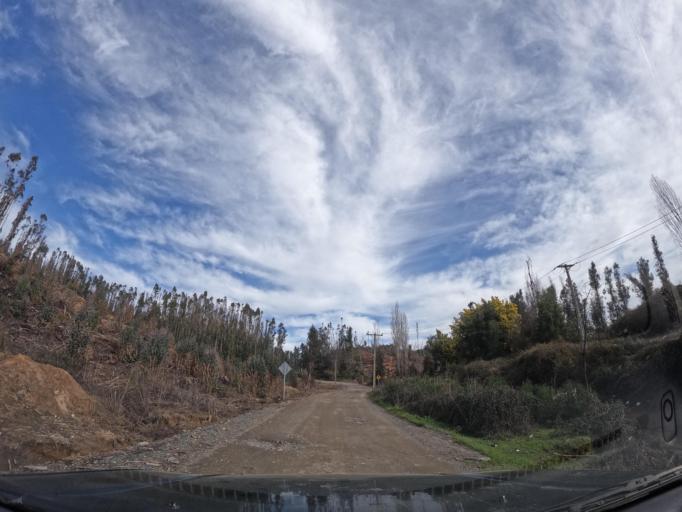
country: CL
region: Biobio
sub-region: Provincia de Concepcion
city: Chiguayante
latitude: -37.0091
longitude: -72.9105
